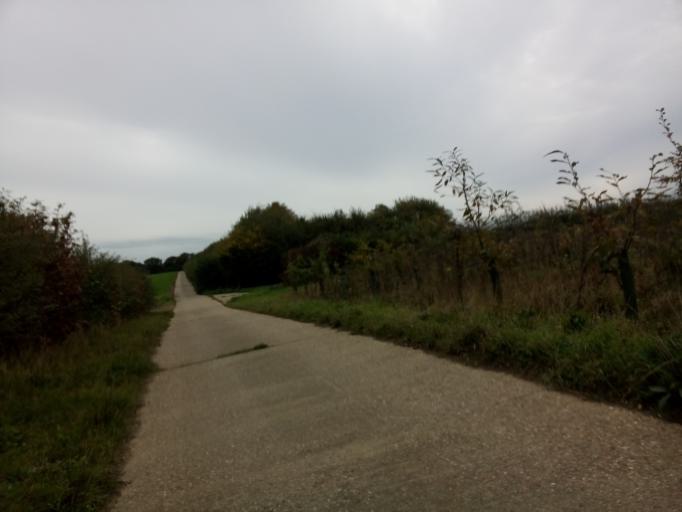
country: GB
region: England
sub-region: Suffolk
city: Ipswich
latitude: 52.0152
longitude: 1.1388
